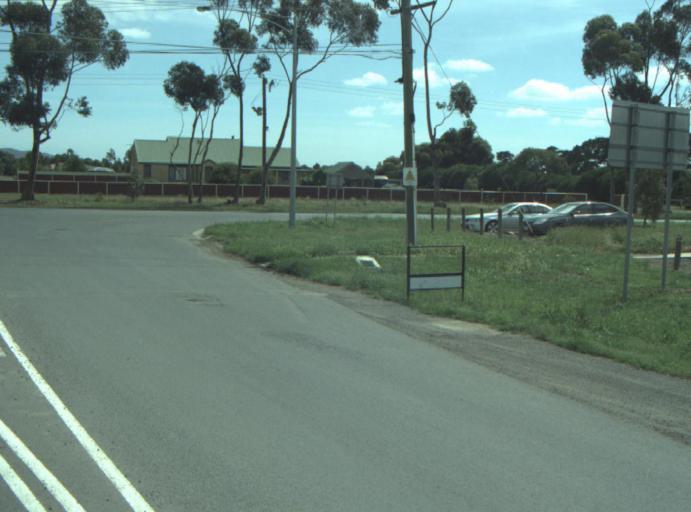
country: AU
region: Victoria
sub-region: Greater Geelong
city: Lara
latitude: -38.0269
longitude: 144.4290
